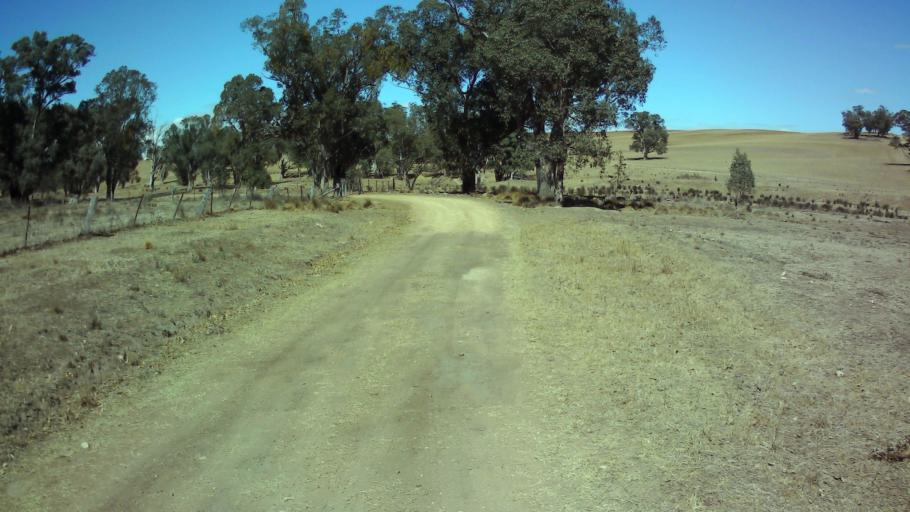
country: AU
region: New South Wales
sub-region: Young
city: Young
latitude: -34.0449
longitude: 148.4256
